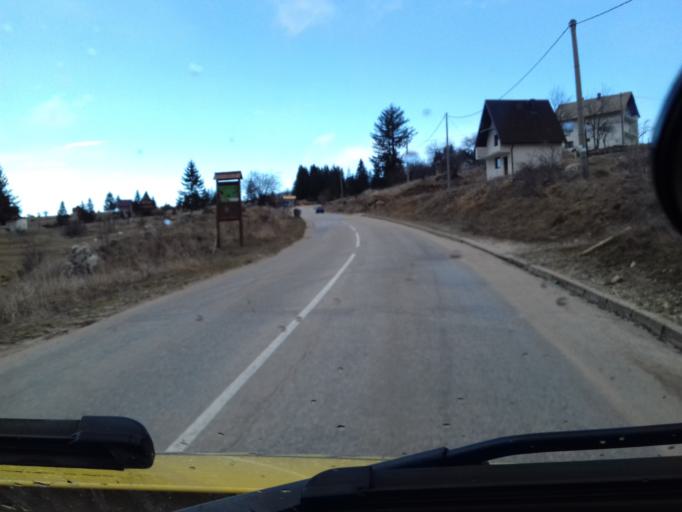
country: BA
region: Federation of Bosnia and Herzegovina
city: Turbe
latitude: 44.3113
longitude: 17.5488
